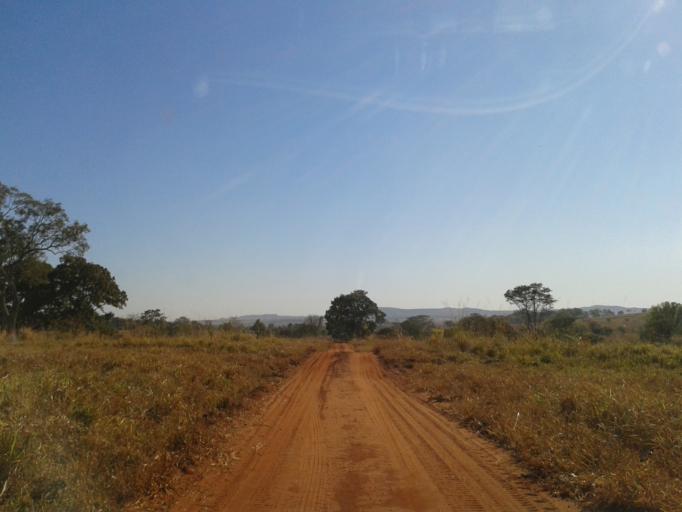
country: BR
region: Minas Gerais
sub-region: Santa Vitoria
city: Santa Vitoria
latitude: -19.0650
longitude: -49.9236
